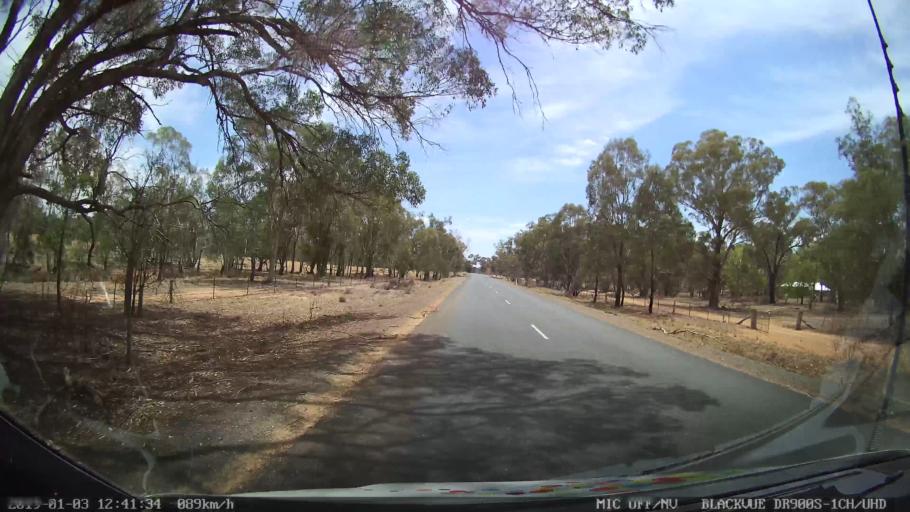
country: AU
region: New South Wales
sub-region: Weddin
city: Grenfell
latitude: -33.7978
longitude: 148.2152
